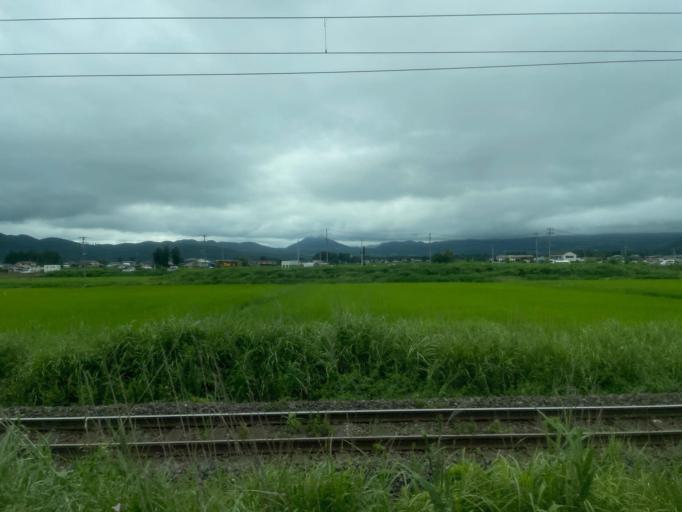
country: JP
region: Fukushima
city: Motomiya
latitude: 37.5356
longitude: 140.3985
